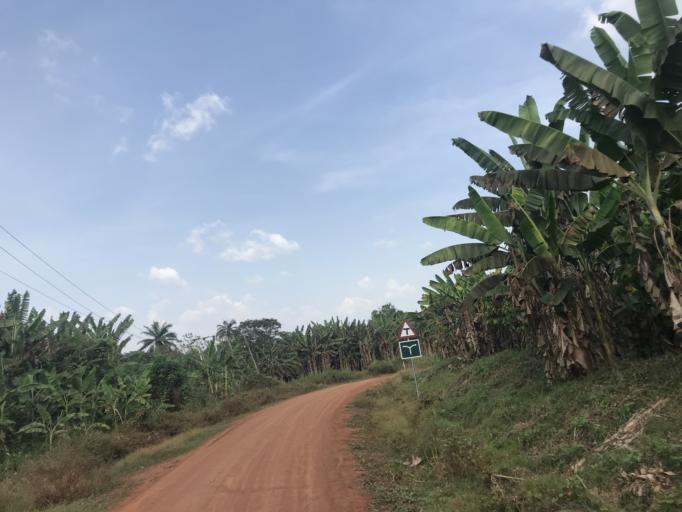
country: NG
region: Osun
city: Ilesa
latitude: 7.6589
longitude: 4.6725
